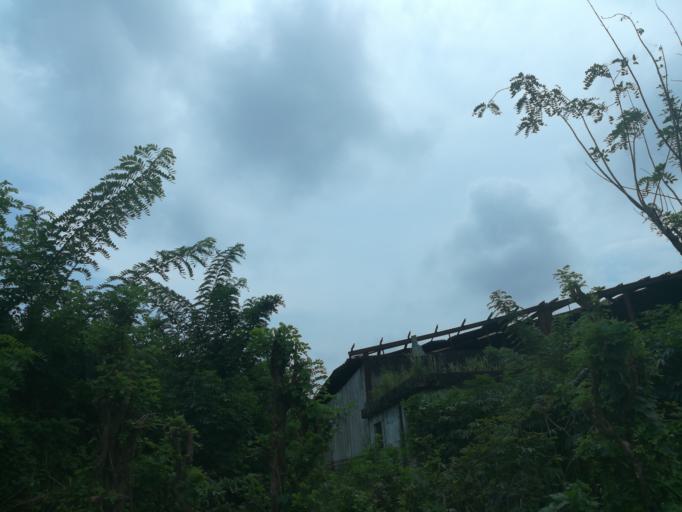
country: NG
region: Lagos
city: Oshodi
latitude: 6.5637
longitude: 3.3576
